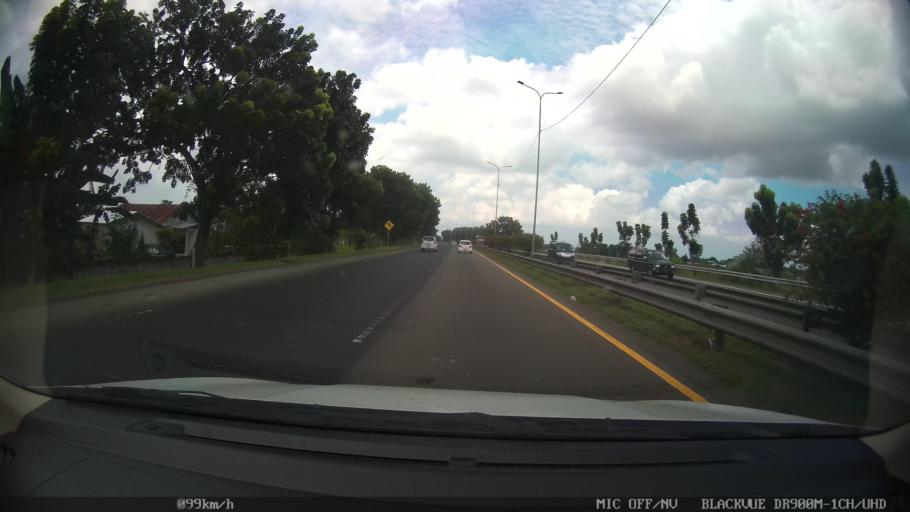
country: ID
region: North Sumatra
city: Medan
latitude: 3.6239
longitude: 98.7196
